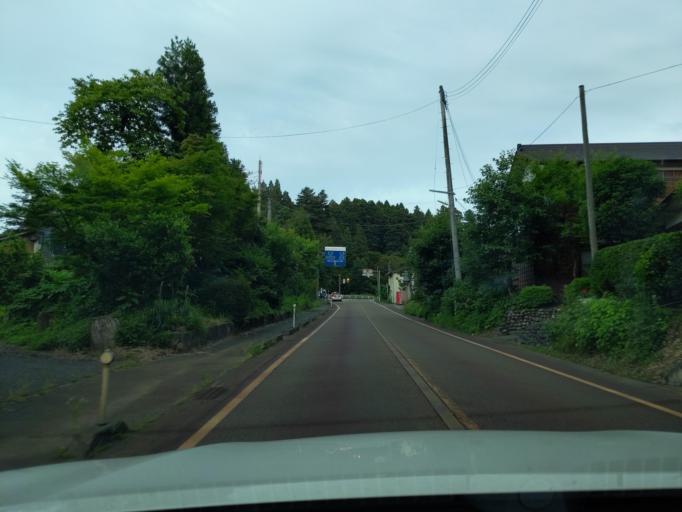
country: JP
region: Niigata
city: Nagaoka
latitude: 37.4345
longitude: 138.7271
